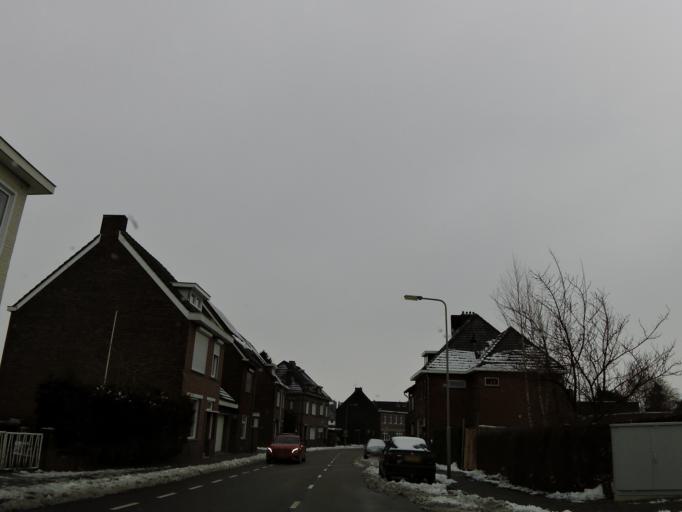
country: NL
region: Limburg
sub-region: Gemeente Simpelveld
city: Simpelveld
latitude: 50.8195
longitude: 6.0061
